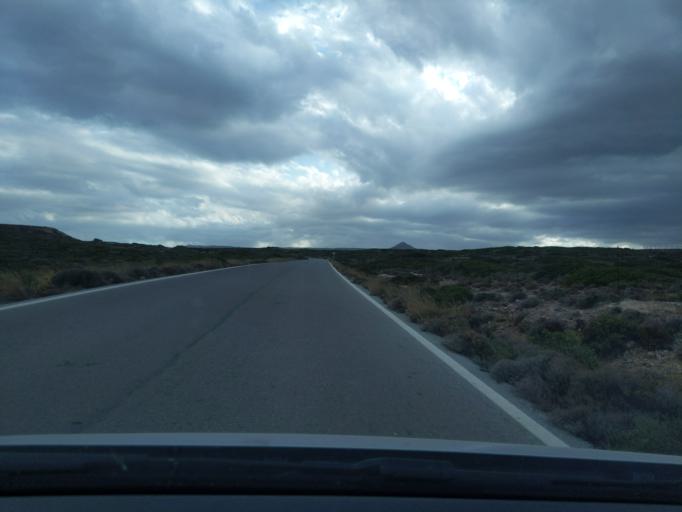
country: GR
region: Crete
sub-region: Nomos Lasithiou
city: Palekastro
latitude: 35.2456
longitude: 26.2495
